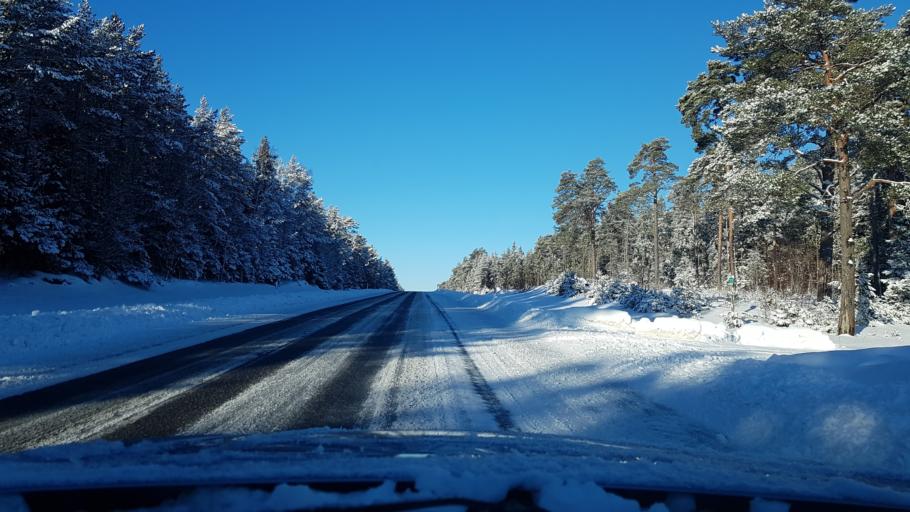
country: EE
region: Hiiumaa
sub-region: Kaerdla linn
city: Kardla
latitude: 58.9588
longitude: 22.8564
